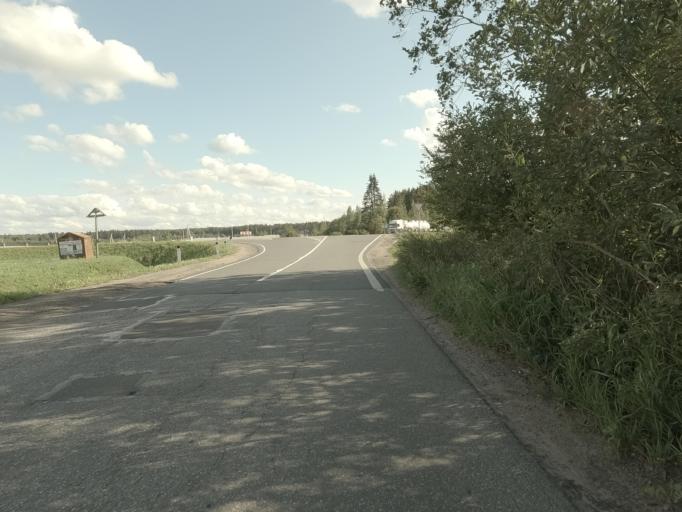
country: RU
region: Leningrad
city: Ul'yanovka
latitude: 59.6273
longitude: 30.7939
